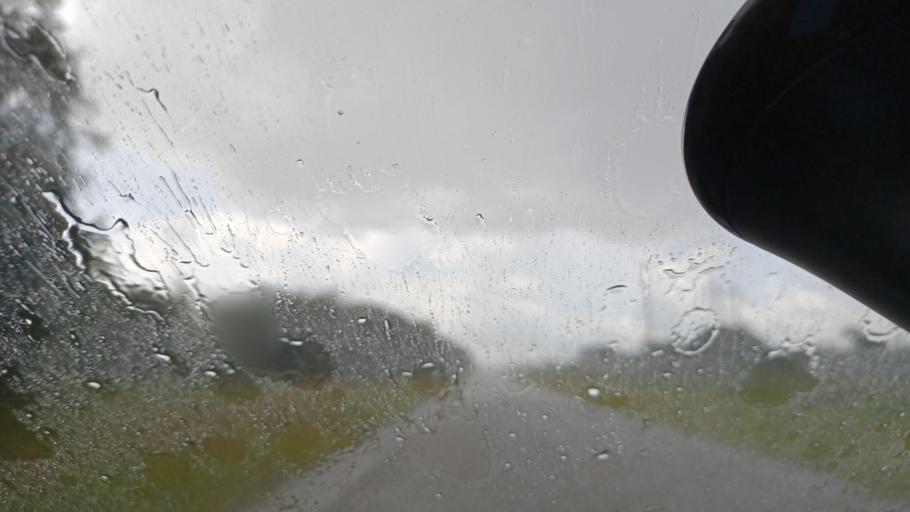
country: ZM
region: North-Western
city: Kasempa
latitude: -13.0958
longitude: 25.9122
